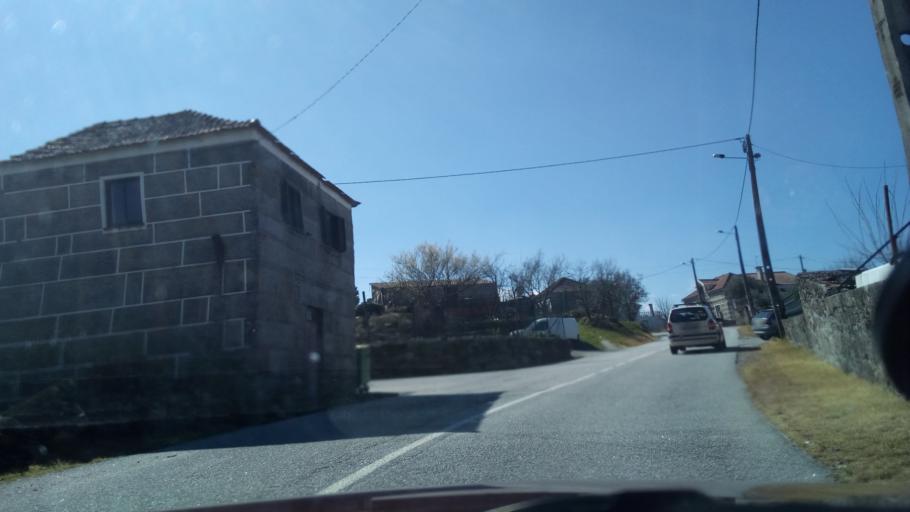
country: PT
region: Guarda
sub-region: Fornos de Algodres
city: Fornos de Algodres
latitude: 40.6557
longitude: -7.5339
